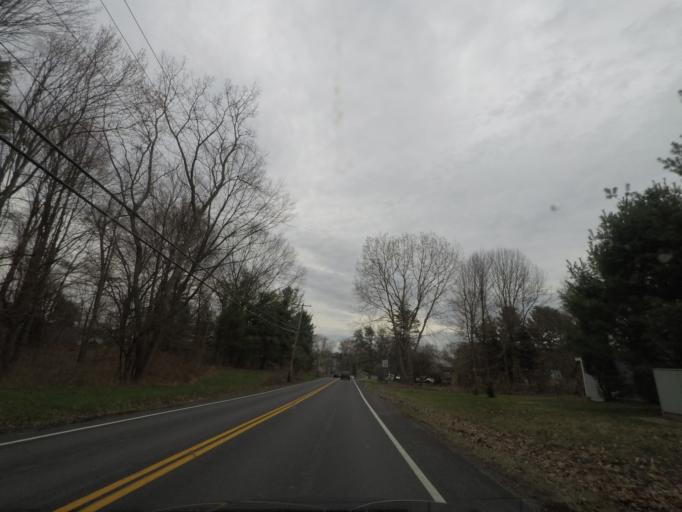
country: US
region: New York
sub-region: Albany County
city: Delmar
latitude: 42.6000
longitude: -73.8224
